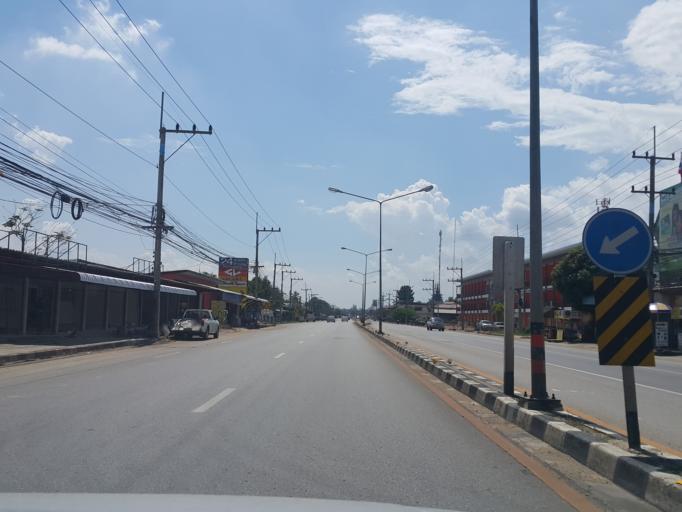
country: TH
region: Chiang Mai
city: Mae Taeng
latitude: 19.0907
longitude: 98.9368
